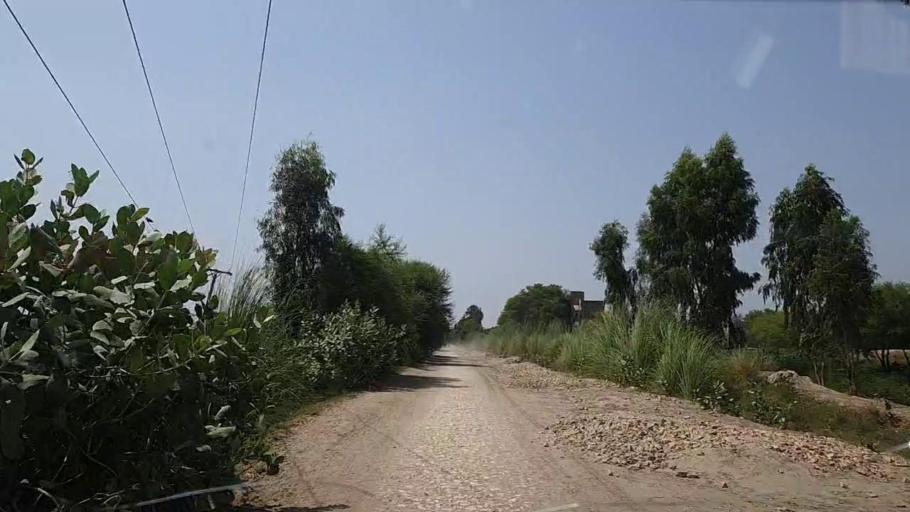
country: PK
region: Sindh
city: Ghotki
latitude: 28.0860
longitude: 69.3384
